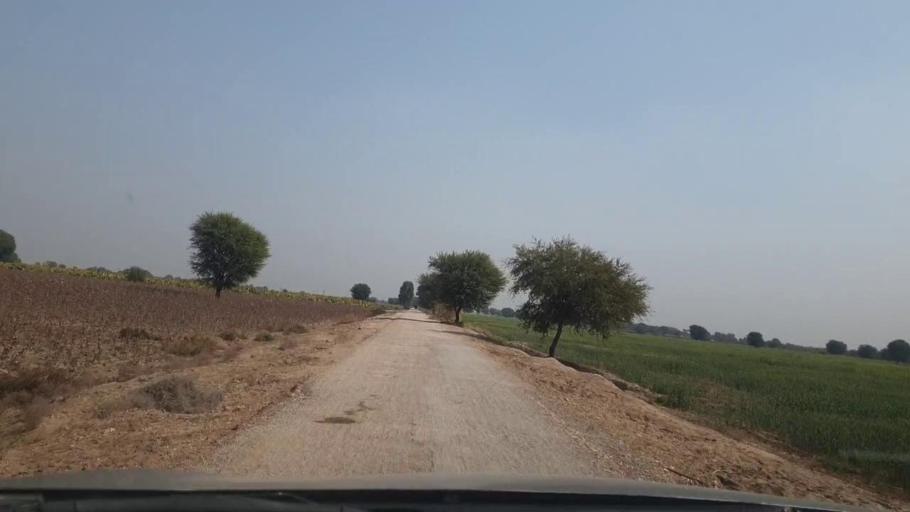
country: PK
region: Sindh
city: Tando Allahyar
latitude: 25.5643
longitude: 68.8080
